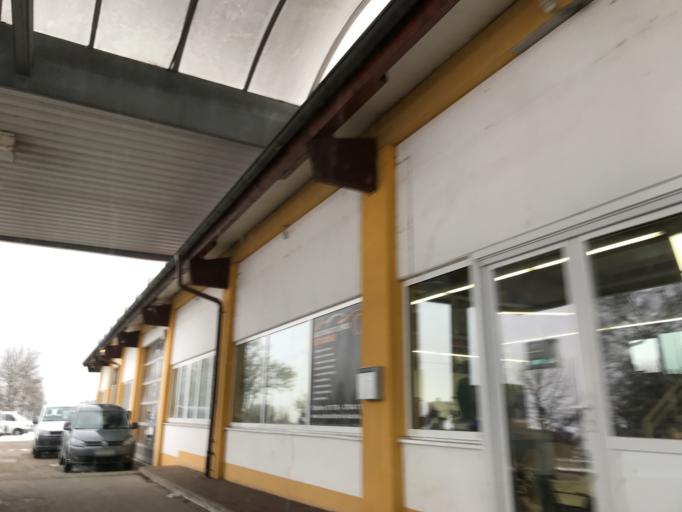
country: DE
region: Baden-Wuerttemberg
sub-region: Freiburg Region
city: Monchweiler
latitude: 48.1050
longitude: 8.4157
